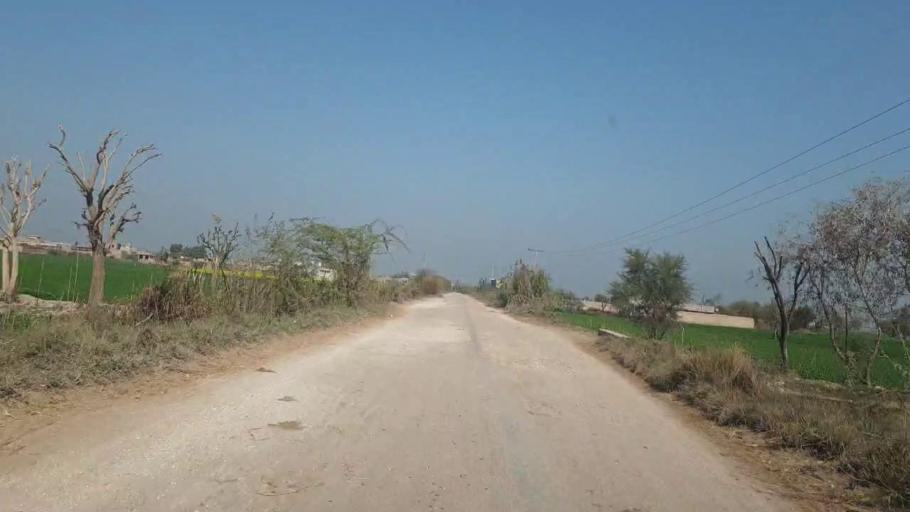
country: PK
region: Sindh
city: Sakrand
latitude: 26.0430
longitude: 68.4024
